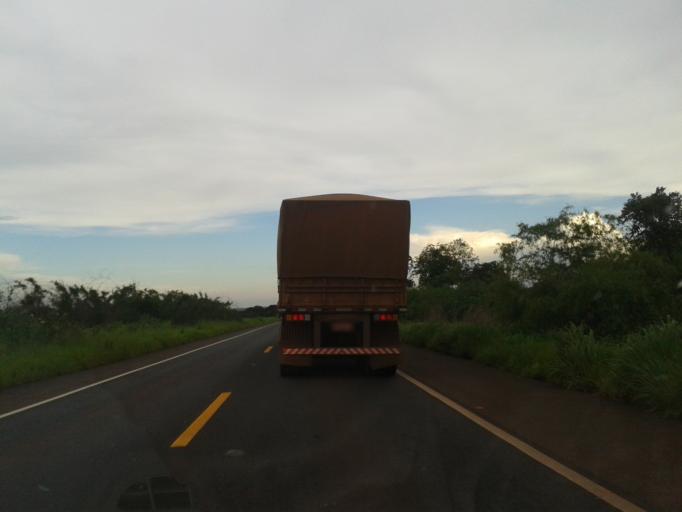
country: BR
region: Minas Gerais
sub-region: Santa Vitoria
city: Santa Vitoria
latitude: -18.8833
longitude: -50.1422
